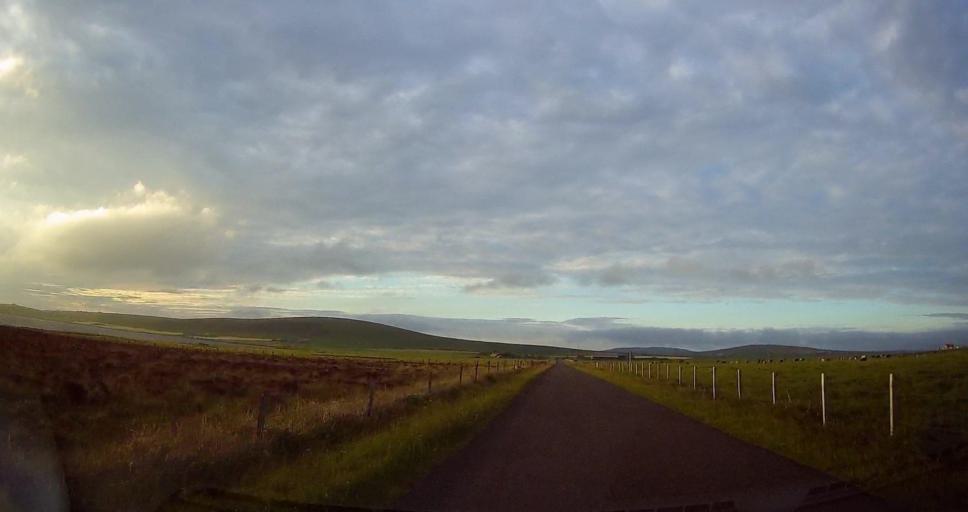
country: GB
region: Scotland
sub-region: Orkney Islands
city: Stromness
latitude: 59.1036
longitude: -3.2576
